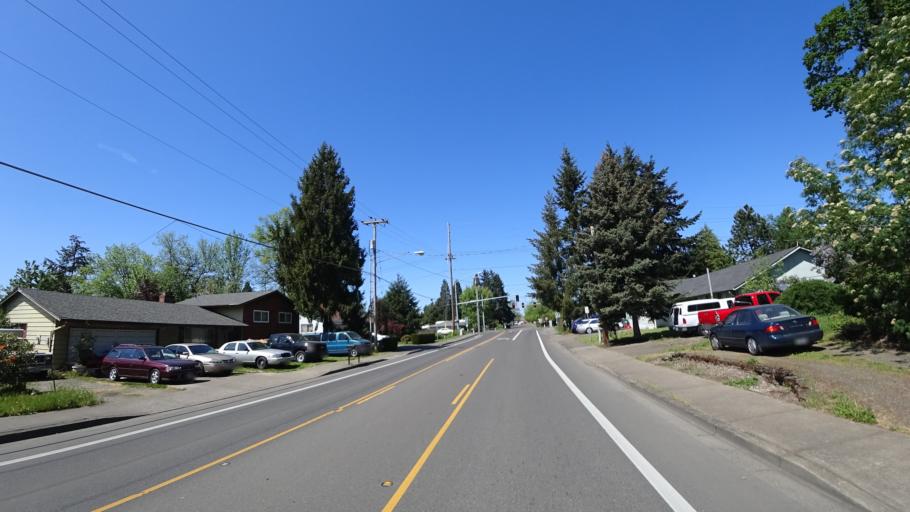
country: US
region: Oregon
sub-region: Washington County
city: Hillsboro
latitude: 45.5192
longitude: -122.9498
